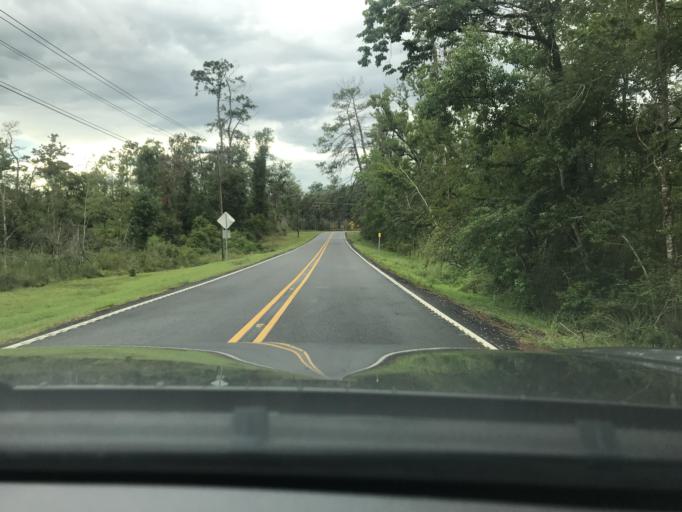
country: US
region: Louisiana
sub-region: Calcasieu Parish
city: Westlake
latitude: 30.3010
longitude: -93.2564
